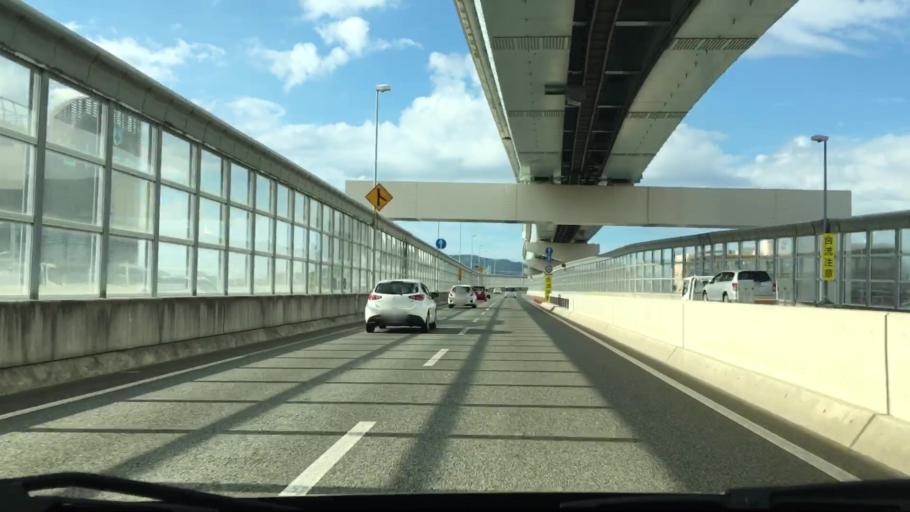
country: JP
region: Fukuoka
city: Fukuoka-shi
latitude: 33.5739
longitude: 130.3162
